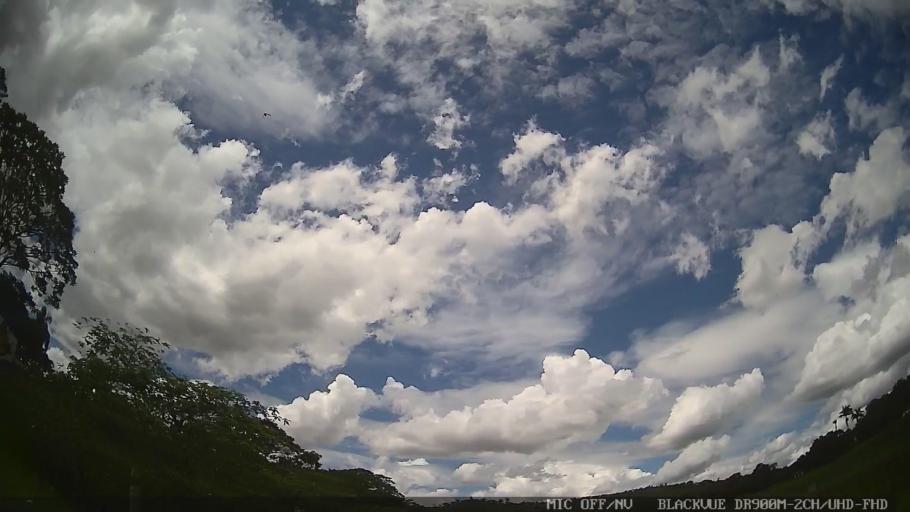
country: BR
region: Sao Paulo
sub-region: Jaguariuna
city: Jaguariuna
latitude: -22.7050
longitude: -46.9797
